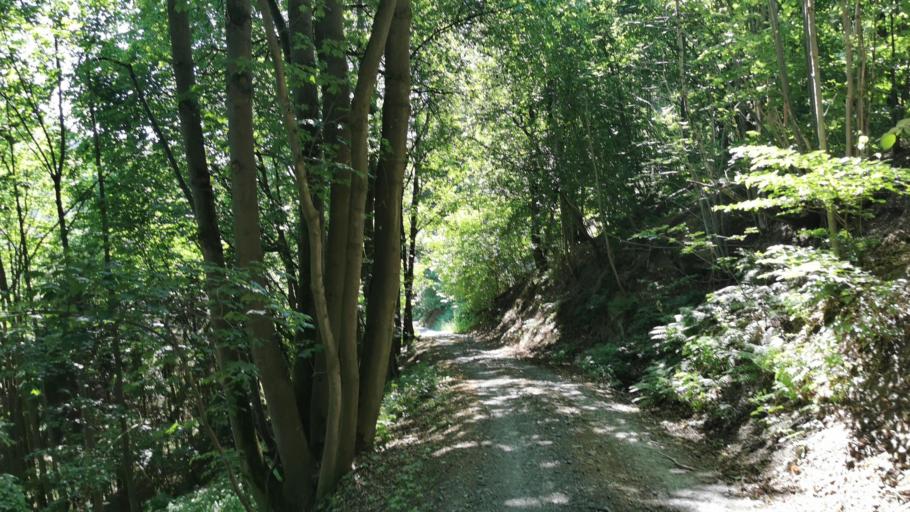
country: DE
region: Thuringia
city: Probstzella
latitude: 50.5415
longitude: 11.3980
